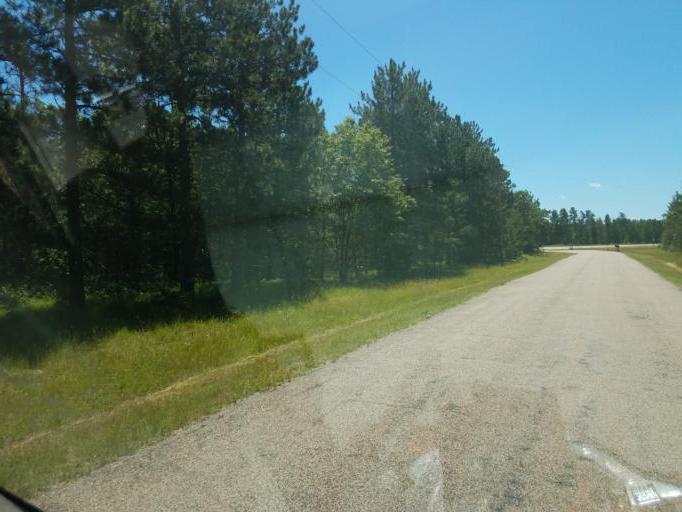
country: US
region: Wisconsin
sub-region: Juneau County
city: New Lisbon
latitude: 44.0451
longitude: -90.0266
